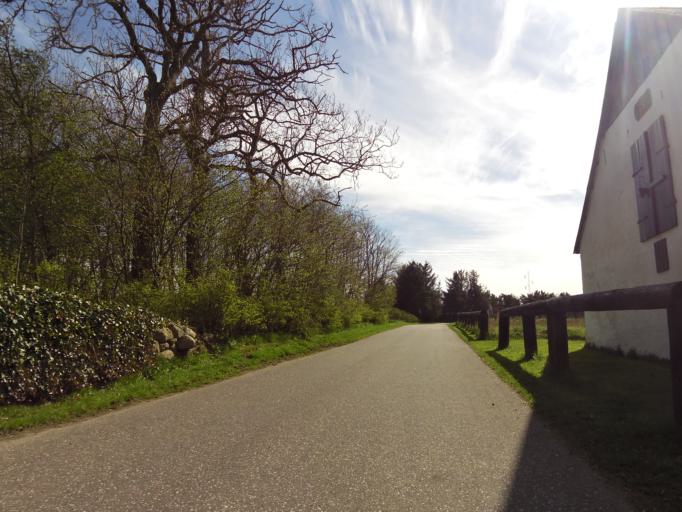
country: DK
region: Central Jutland
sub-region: Skive Kommune
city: Skive
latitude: 56.5648
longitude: 8.9857
